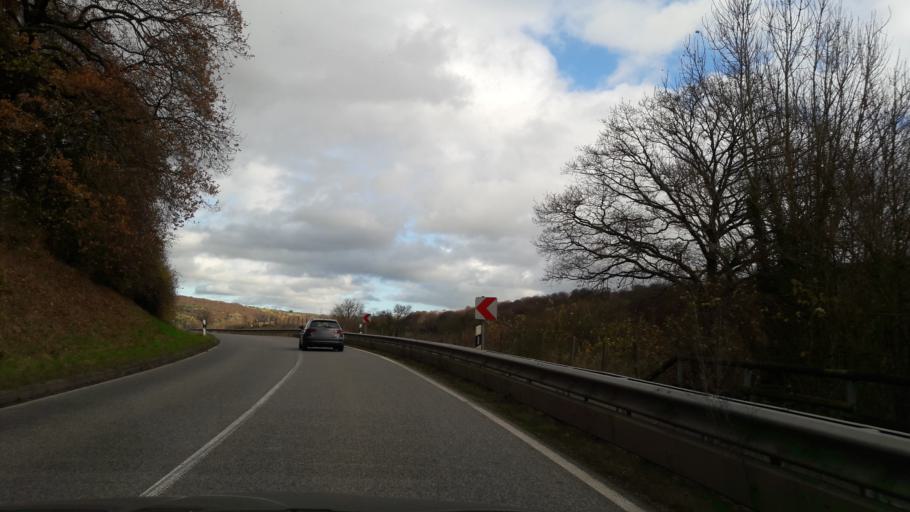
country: DE
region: Rheinland-Pfalz
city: Echternacherbruck
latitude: 49.8122
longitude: 6.4530
